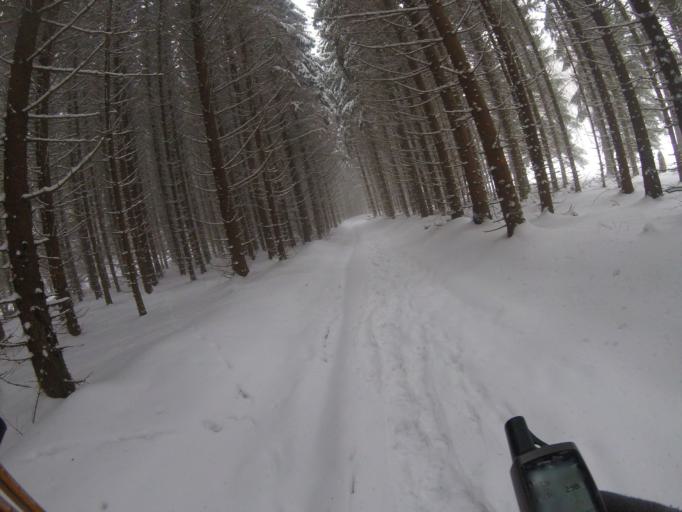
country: HU
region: Heves
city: Szilvasvarad
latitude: 48.0568
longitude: 20.4280
